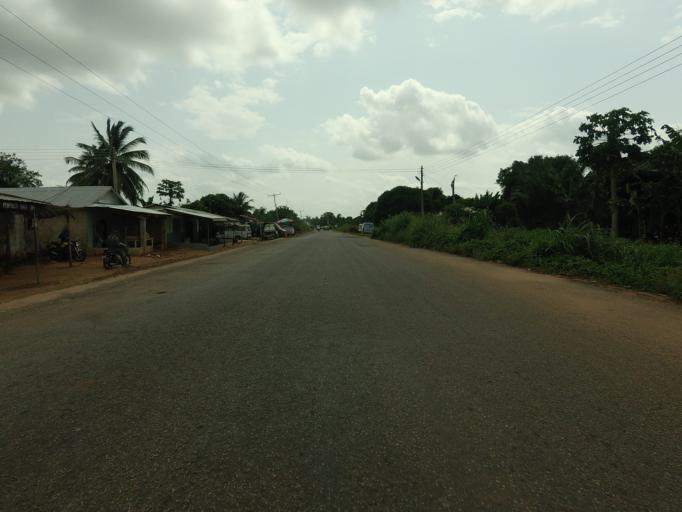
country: TG
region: Maritime
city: Lome
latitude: 6.2232
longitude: 1.0316
